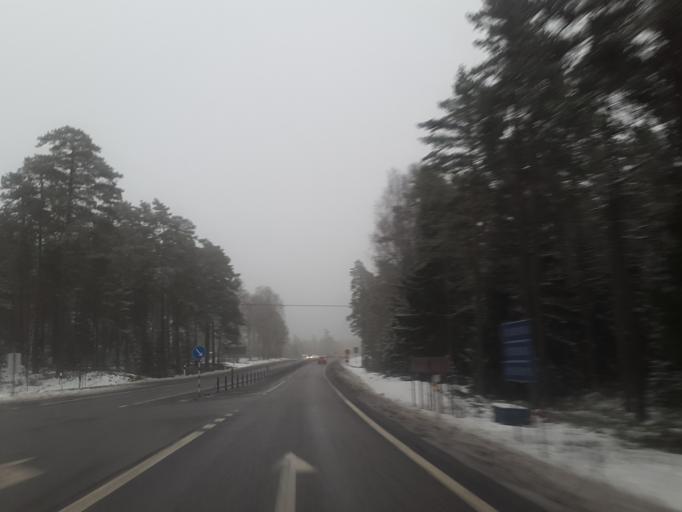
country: SE
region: Joenkoeping
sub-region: Mullsjo Kommun
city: Mullsjoe
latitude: 57.7637
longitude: 13.8289
